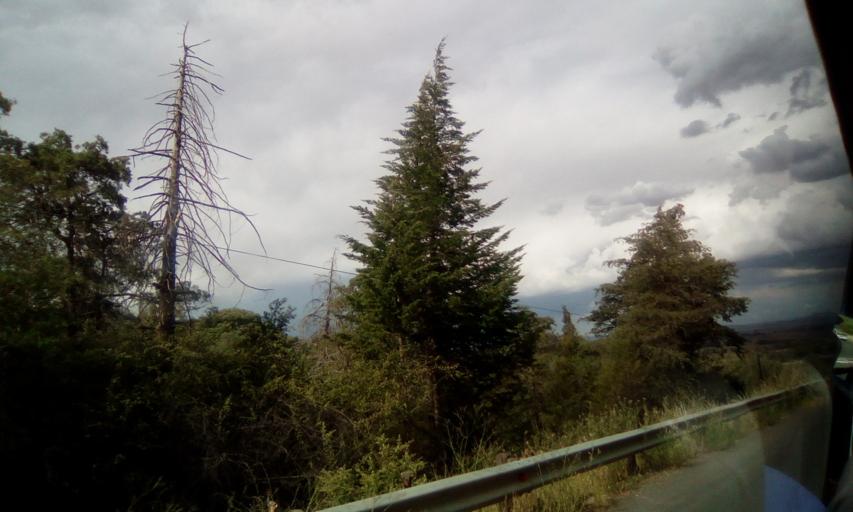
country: ZA
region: Orange Free State
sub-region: Thabo Mofutsanyana District Municipality
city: Ladybrand
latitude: -29.2127
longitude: 27.4558
